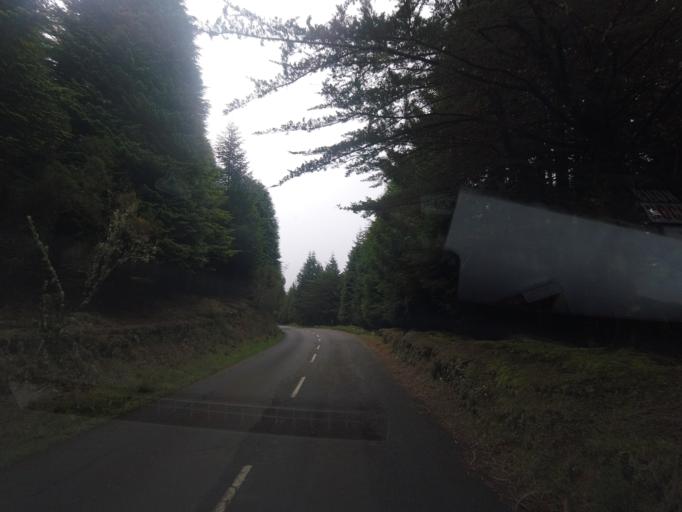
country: PT
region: Madeira
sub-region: Santa Cruz
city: Camacha
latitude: 32.7195
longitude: -16.8649
